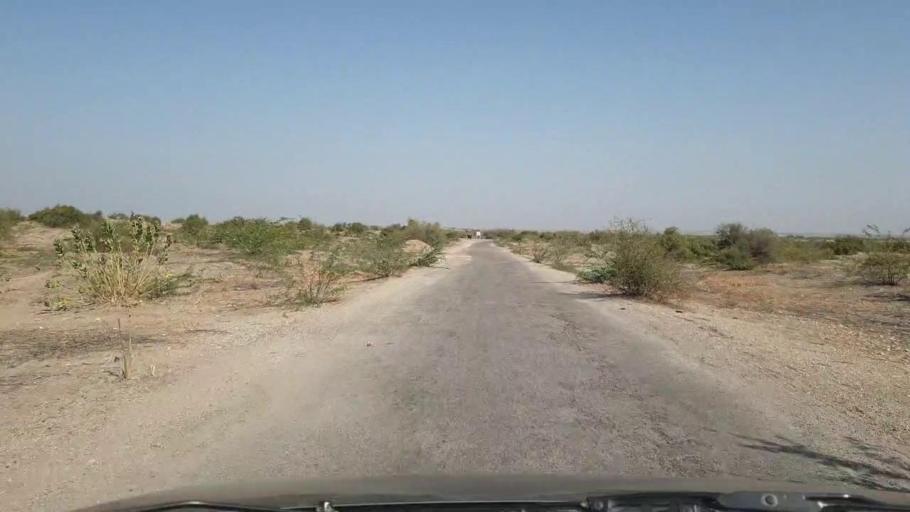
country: PK
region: Sindh
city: Chor
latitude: 25.5180
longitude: 69.8180
